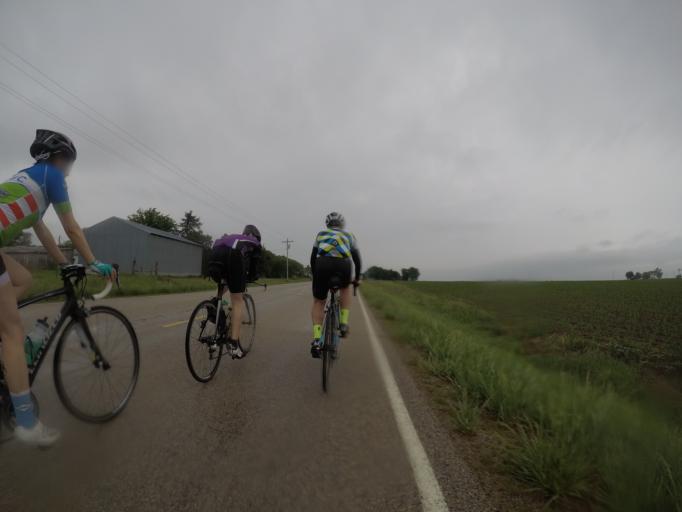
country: US
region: Kansas
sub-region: Pottawatomie County
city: Wamego
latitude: 39.3498
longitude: -96.2211
